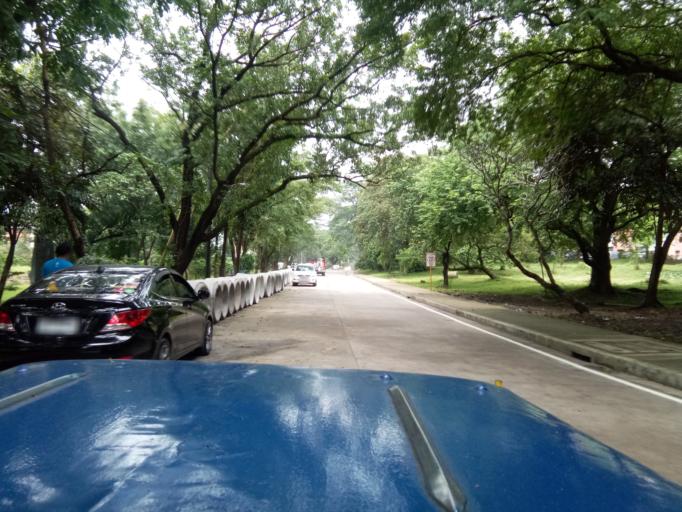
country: PH
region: Metro Manila
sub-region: Quezon City
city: Quezon City
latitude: 14.6504
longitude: 121.0666
